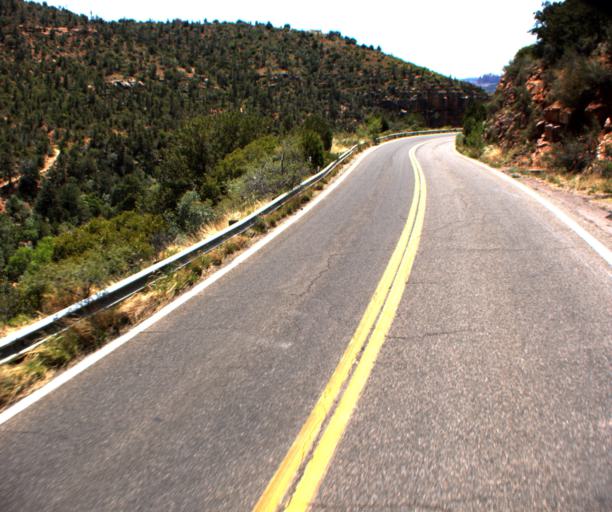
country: US
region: Arizona
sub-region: Coconino County
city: Sedona
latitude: 34.8800
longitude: -111.7491
